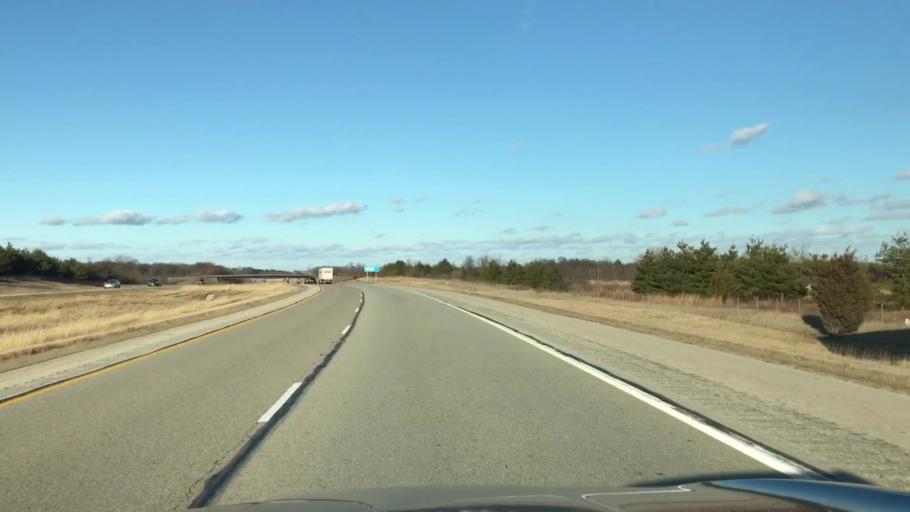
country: US
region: Illinois
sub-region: McLean County
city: Lexington
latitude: 40.6204
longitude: -88.8190
